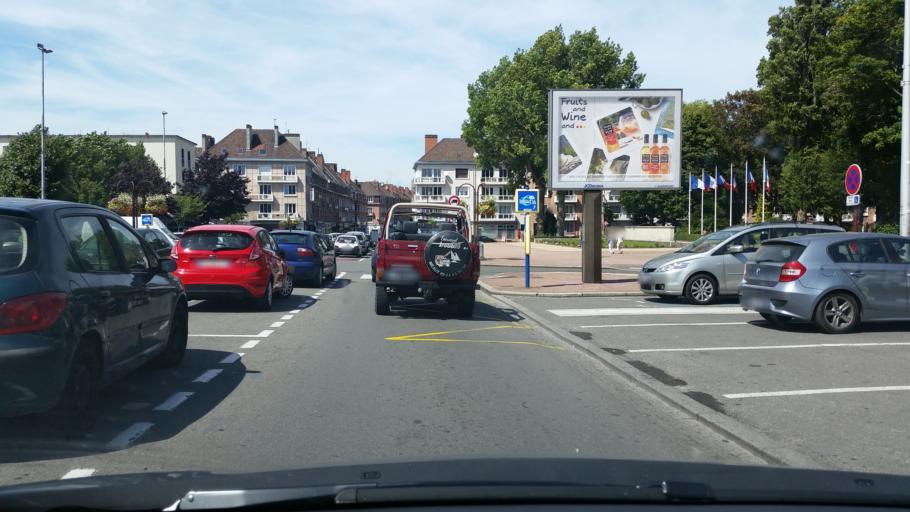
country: FR
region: Nord-Pas-de-Calais
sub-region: Departement du Pas-de-Calais
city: Calais
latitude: 50.9553
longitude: 1.8504
